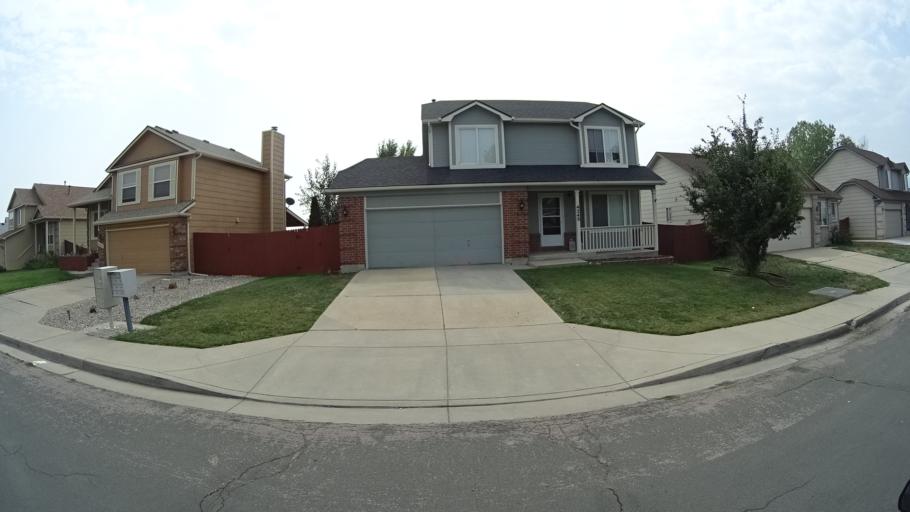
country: US
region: Colorado
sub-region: El Paso County
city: Stratmoor
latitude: 38.8207
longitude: -104.7482
